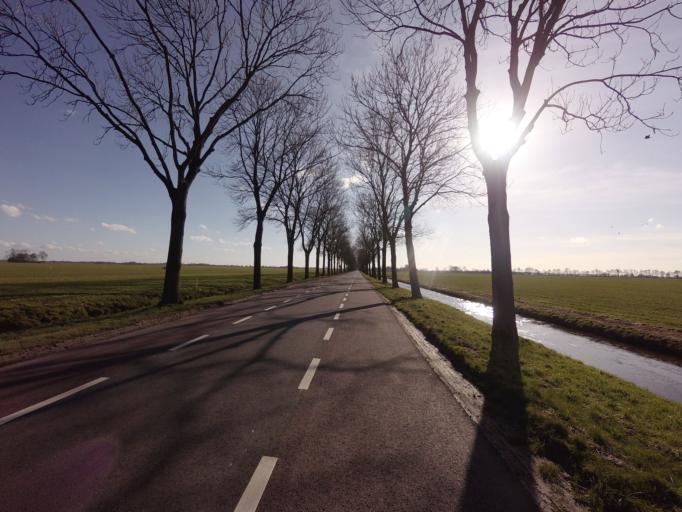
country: NL
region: Utrecht
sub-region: Gemeente Montfoort
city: Montfoort
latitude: 52.0758
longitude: 4.9590
